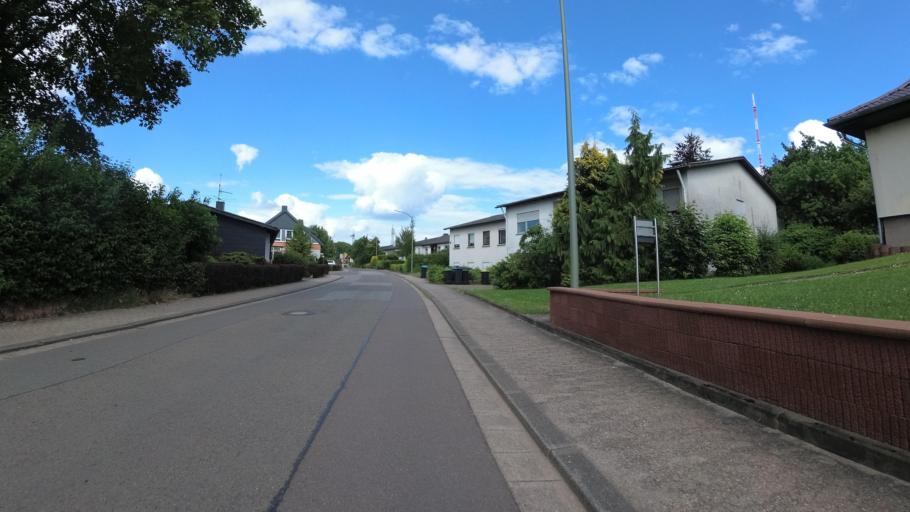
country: DE
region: Saarland
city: Riegelsberg
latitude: 49.2933
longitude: 6.9103
